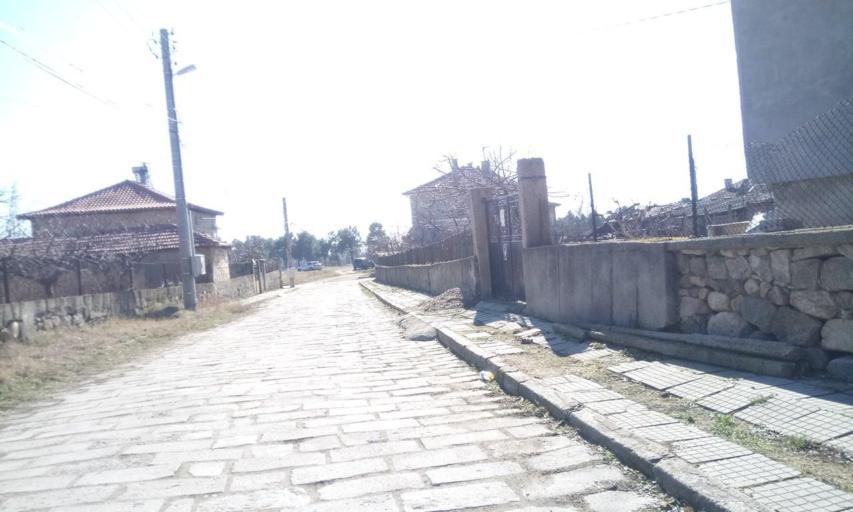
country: BG
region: Plovdiv
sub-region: Obshtina Khisarya
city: Khisarya
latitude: 42.5185
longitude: 24.7213
